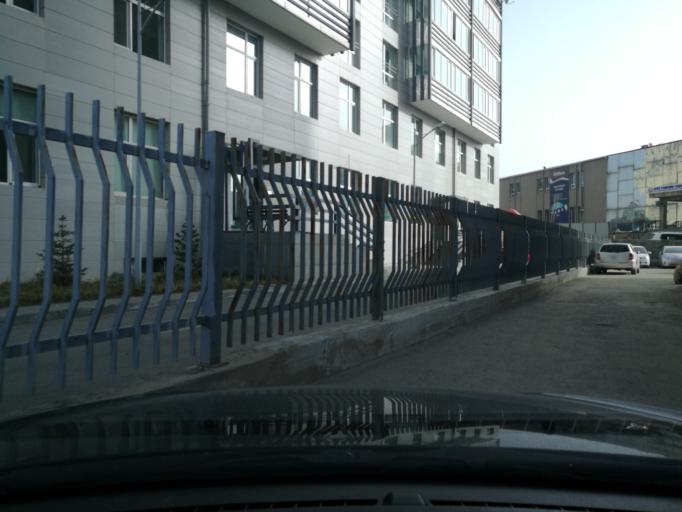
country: MN
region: Ulaanbaatar
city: Ulaanbaatar
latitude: 47.9111
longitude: 106.9060
